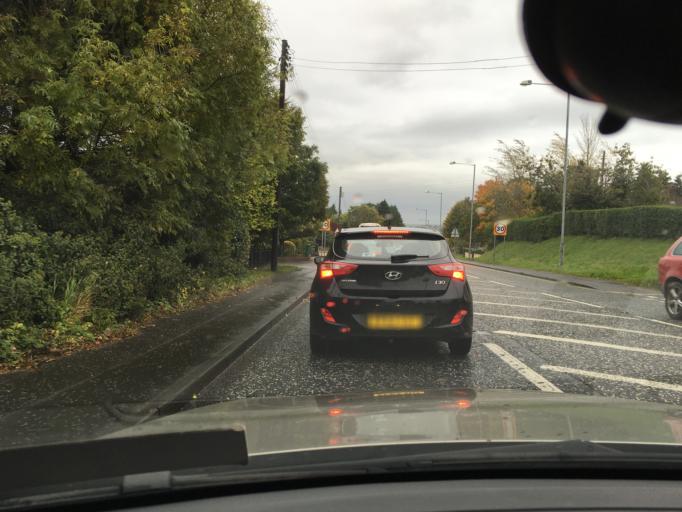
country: GB
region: Northern Ireland
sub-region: Newry and Mourne District
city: Newry
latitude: 54.1629
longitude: -6.3454
